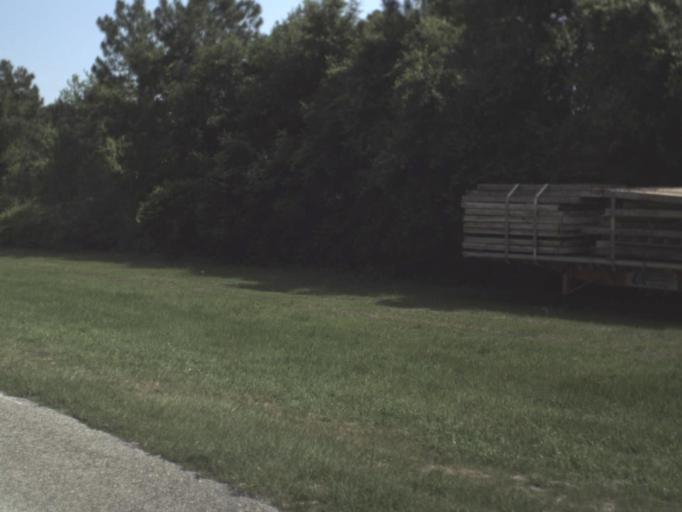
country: US
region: Florida
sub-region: Saint Johns County
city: Palm Valley
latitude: 30.0885
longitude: -81.4626
